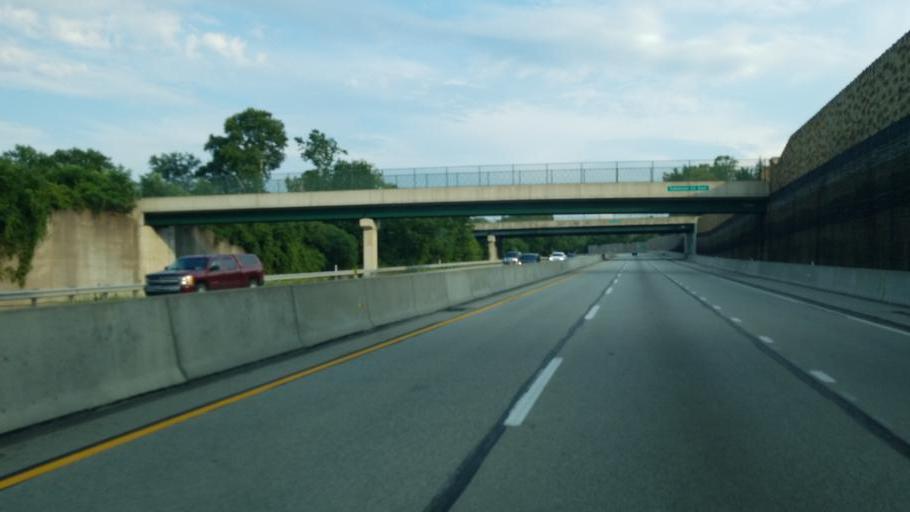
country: US
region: Pennsylvania
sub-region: Allegheny County
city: Oakmont
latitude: 40.5276
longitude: -79.8212
